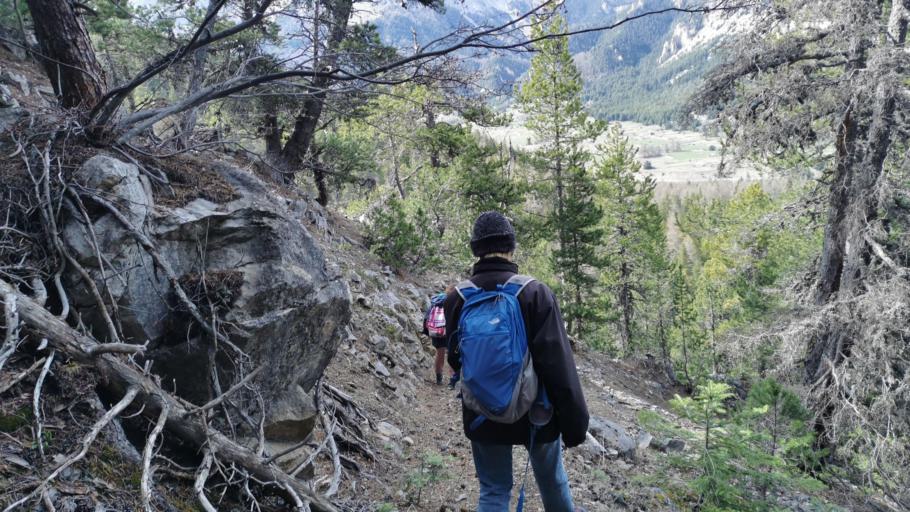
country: IT
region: Piedmont
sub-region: Provincia di Torino
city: Bardonecchia
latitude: 45.0093
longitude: 6.6468
